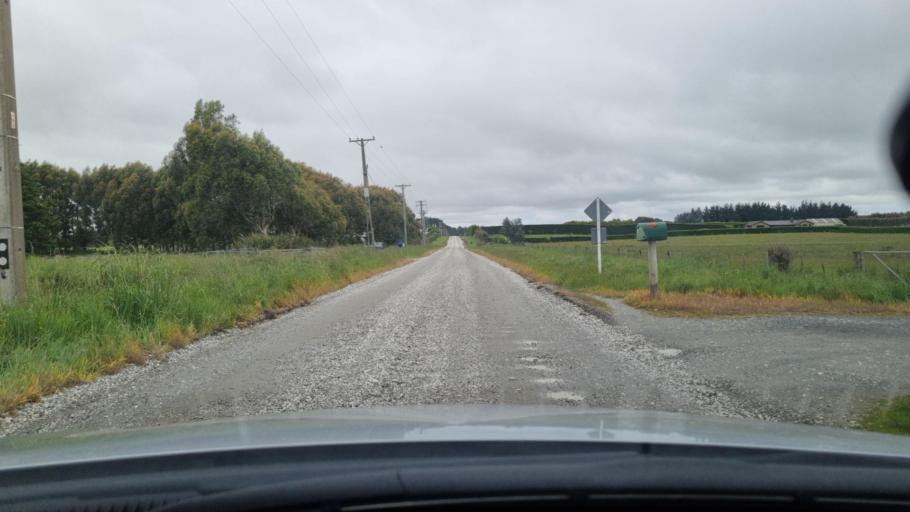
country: NZ
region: Southland
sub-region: Invercargill City
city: Invercargill
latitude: -46.4111
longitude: 168.4403
